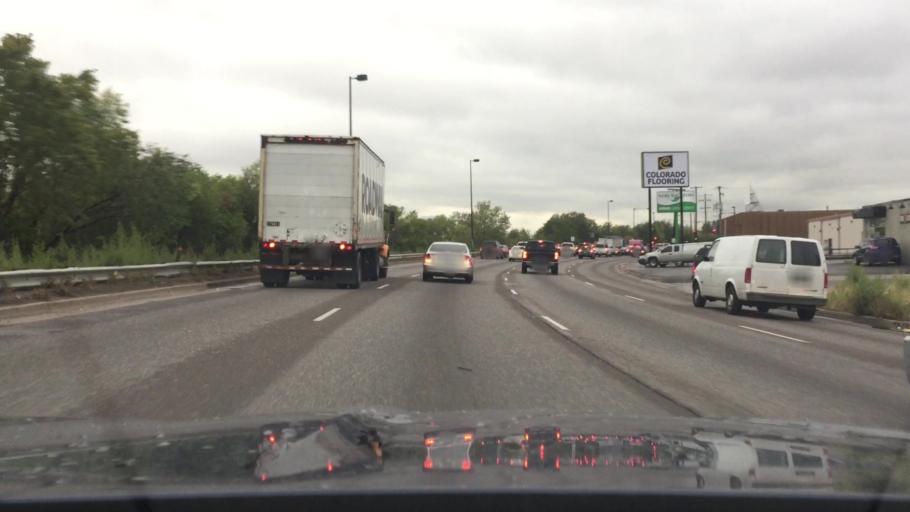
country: US
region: Colorado
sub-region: Denver County
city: Denver
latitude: 39.6988
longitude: -104.9928
